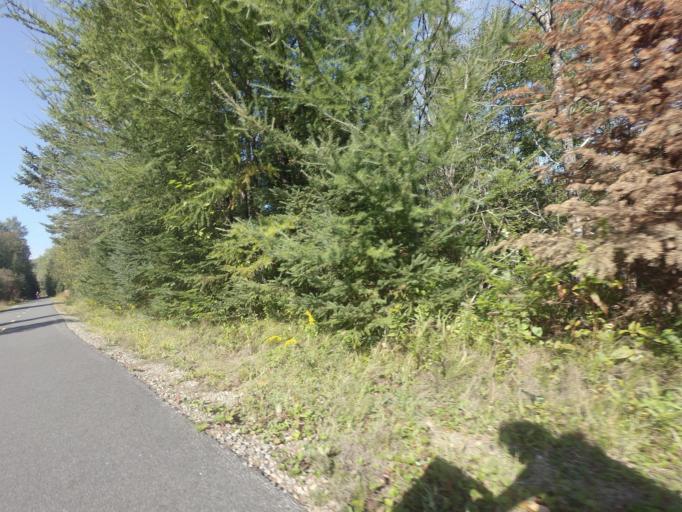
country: CA
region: Quebec
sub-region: Laurentides
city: Mont-Tremblant
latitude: 46.1271
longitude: -74.5476
